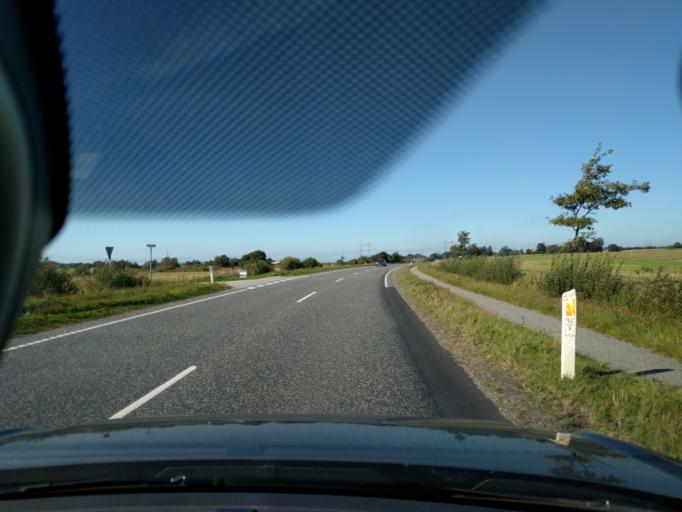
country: DK
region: North Denmark
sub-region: Vesthimmerland Kommune
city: Alestrup
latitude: 56.7130
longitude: 9.6177
